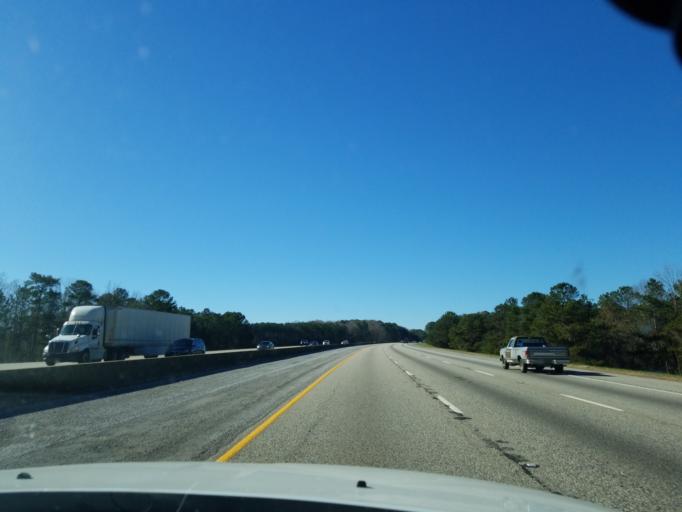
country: US
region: Alabama
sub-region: Shelby County
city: Helena
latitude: 33.3424
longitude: -86.8834
